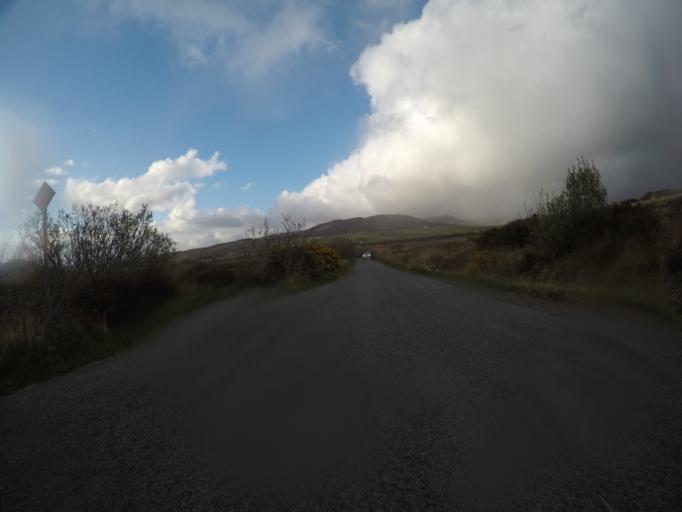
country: GB
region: Scotland
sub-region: Highland
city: Portree
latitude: 57.4705
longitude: -6.2996
